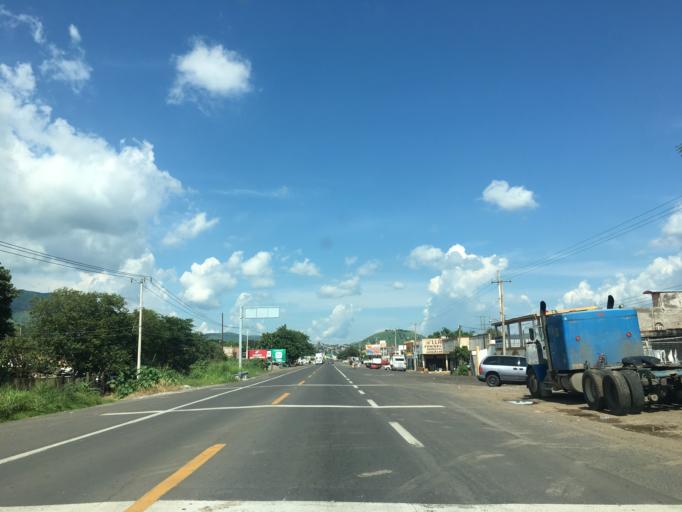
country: MX
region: Nayarit
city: Ixtlan del Rio
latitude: 21.0374
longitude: -104.3885
